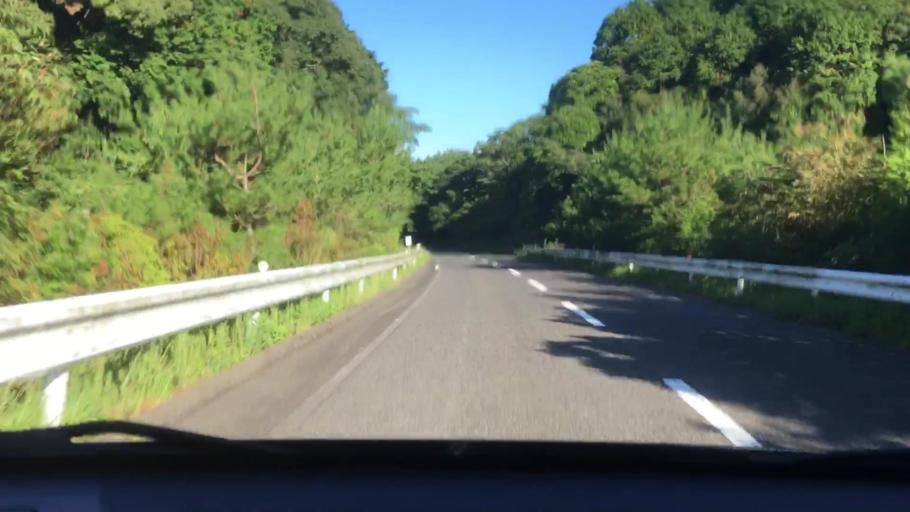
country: JP
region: Nagasaki
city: Sasebo
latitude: 33.0245
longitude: 129.6976
